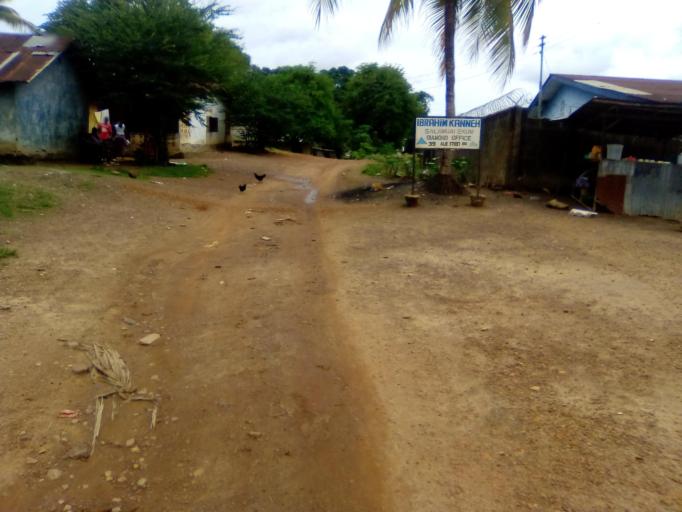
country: SL
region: Southern Province
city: Bo
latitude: 7.9469
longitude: -11.7262
